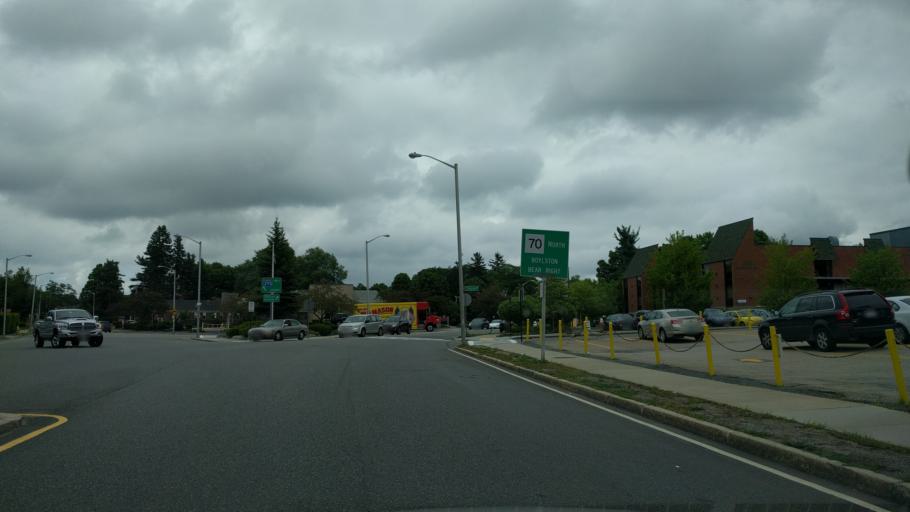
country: US
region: Massachusetts
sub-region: Worcester County
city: Worcester
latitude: 42.2862
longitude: -71.7908
